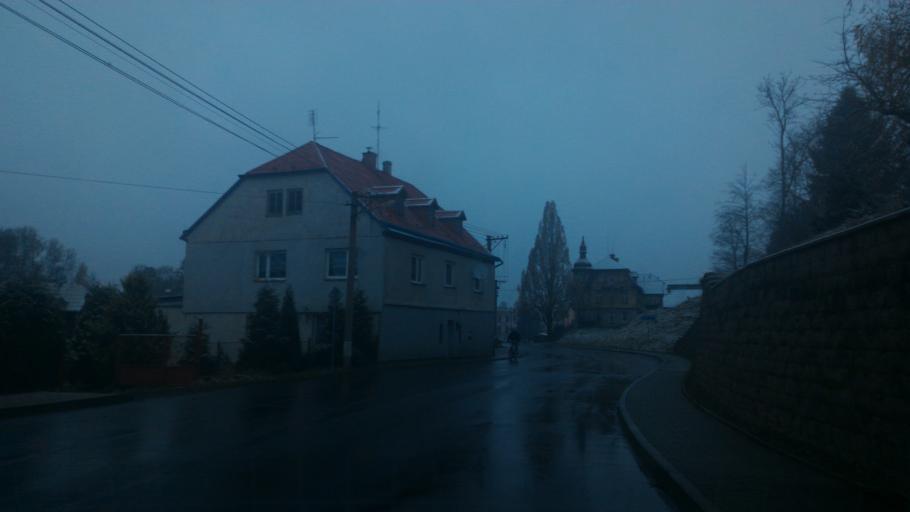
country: CZ
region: Ustecky
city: Jirikov
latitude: 50.9921
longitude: 14.5682
